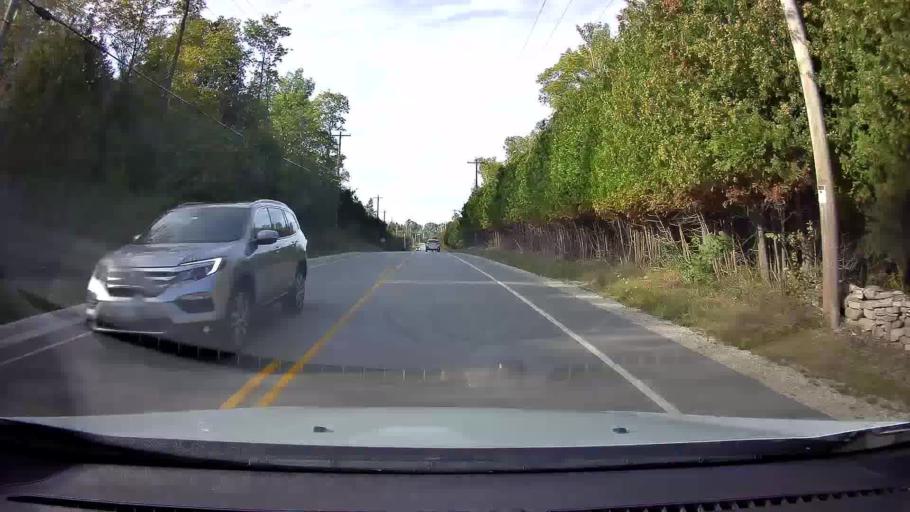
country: US
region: Wisconsin
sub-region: Door County
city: Sturgeon Bay
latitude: 45.1649
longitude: -87.1324
